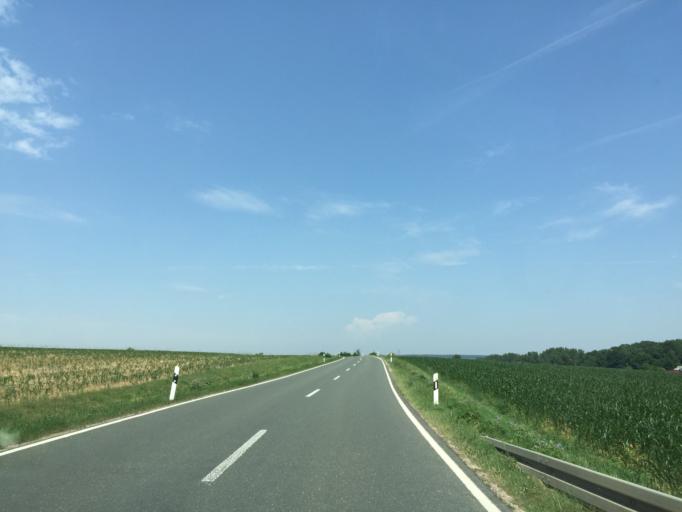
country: DE
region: Thuringia
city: Barchfeld
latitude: 50.7929
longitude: 11.1877
